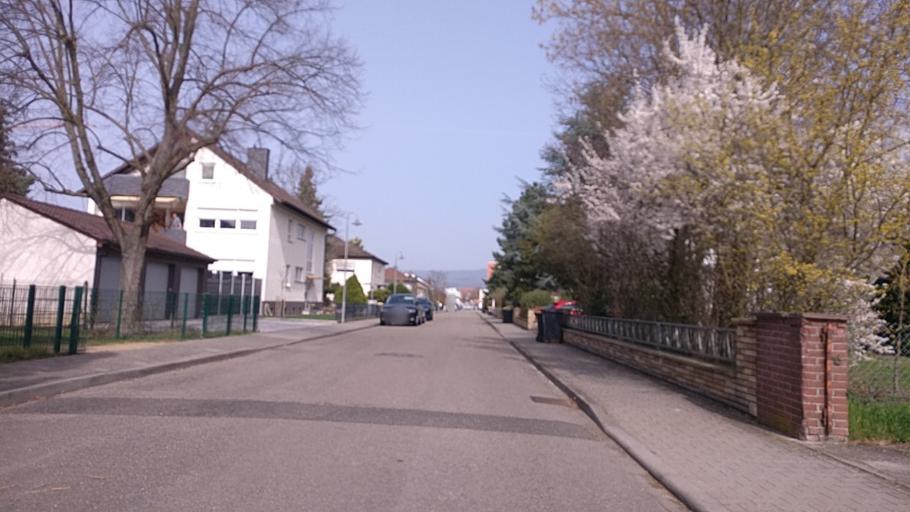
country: DE
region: Rheinland-Pfalz
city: Ingelheim am Rhein
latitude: 49.9704
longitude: 8.0363
